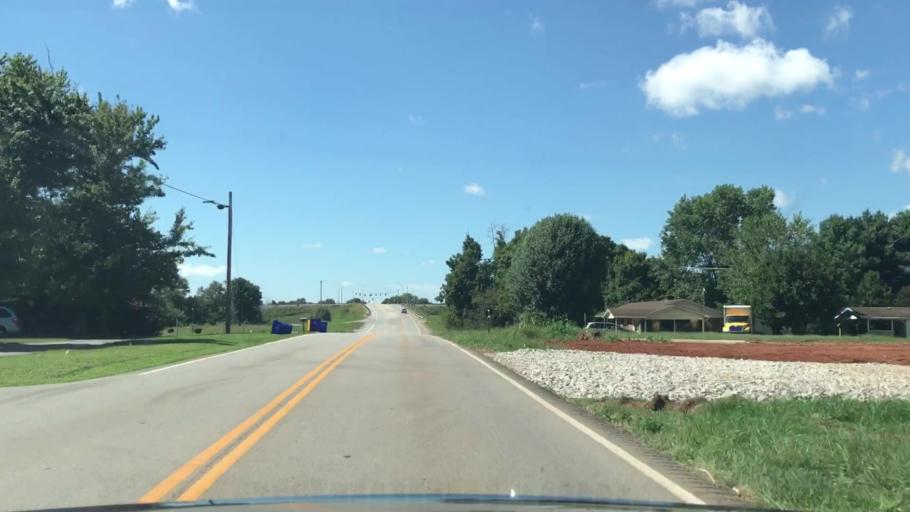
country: US
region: Kentucky
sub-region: Warren County
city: Plano
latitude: 36.9117
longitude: -86.4152
